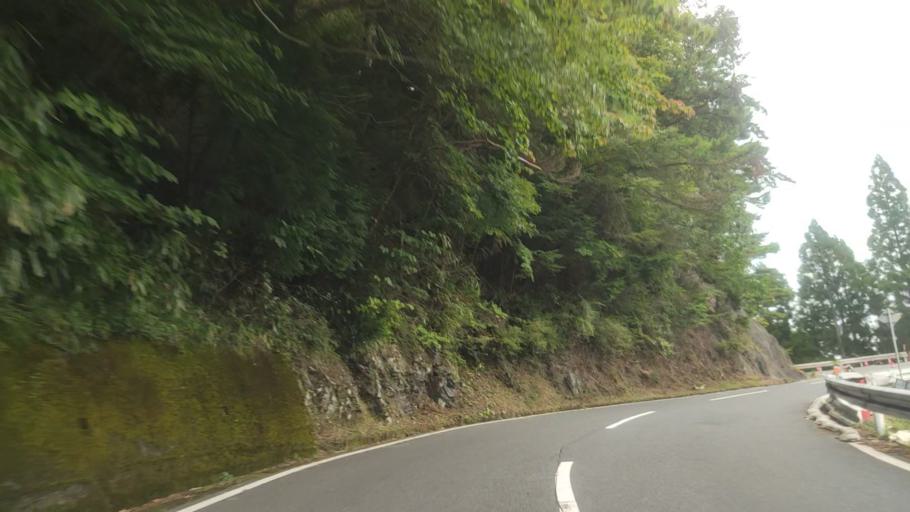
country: JP
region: Wakayama
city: Koya
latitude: 34.2172
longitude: 135.5680
